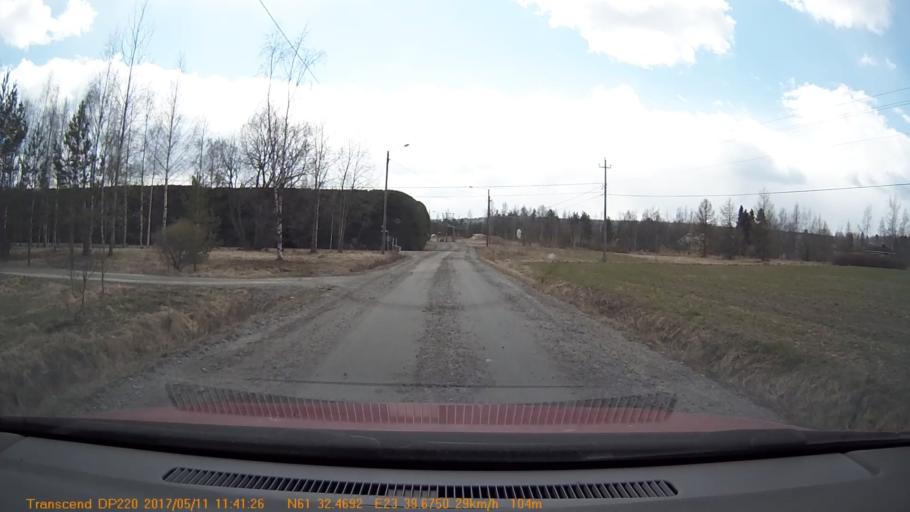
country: FI
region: Pirkanmaa
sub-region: Tampere
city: Yloejaervi
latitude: 61.5412
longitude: 23.6614
